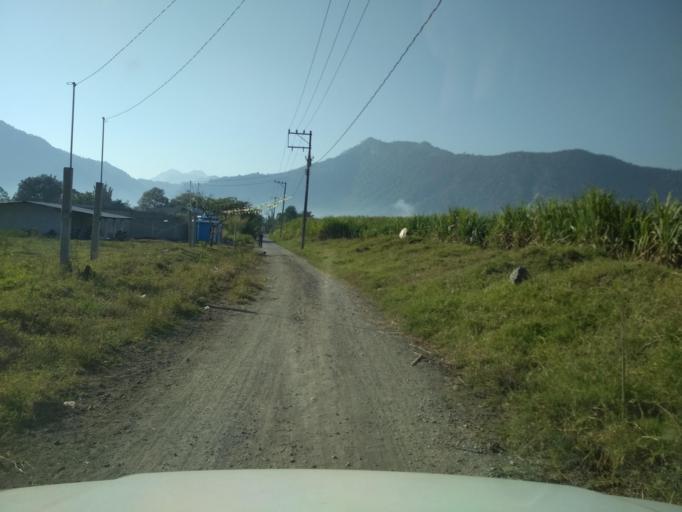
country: MX
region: Veracruz
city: Jalapilla
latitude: 18.8282
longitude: -97.0800
